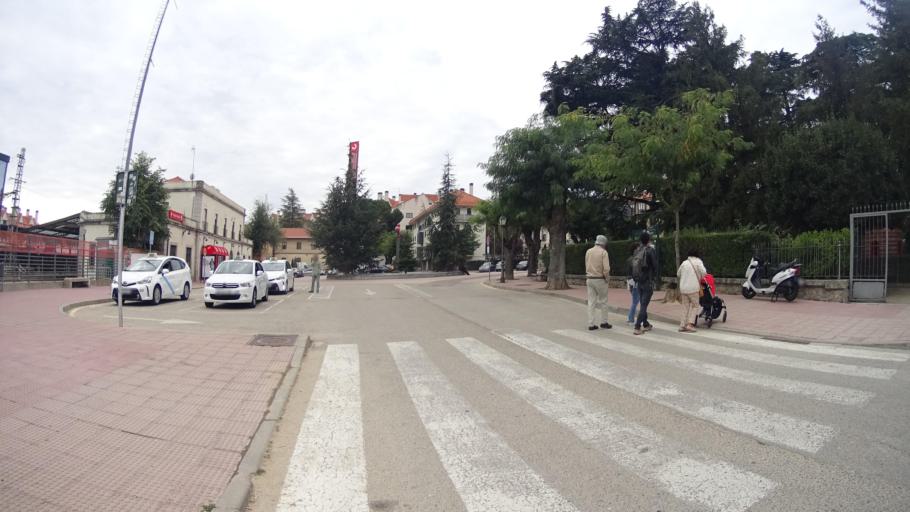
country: ES
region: Madrid
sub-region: Provincia de Madrid
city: El Escorial
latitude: 40.5856
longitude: -4.1327
